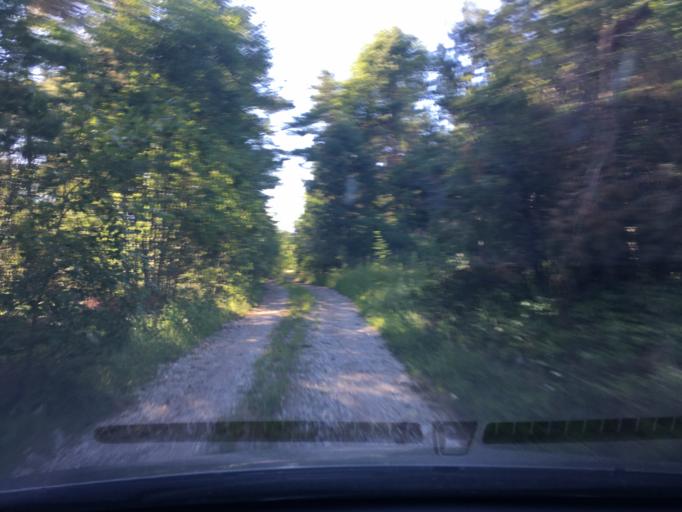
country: EE
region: Laeaene
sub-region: Lihula vald
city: Lihula
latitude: 58.5870
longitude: 23.7463
